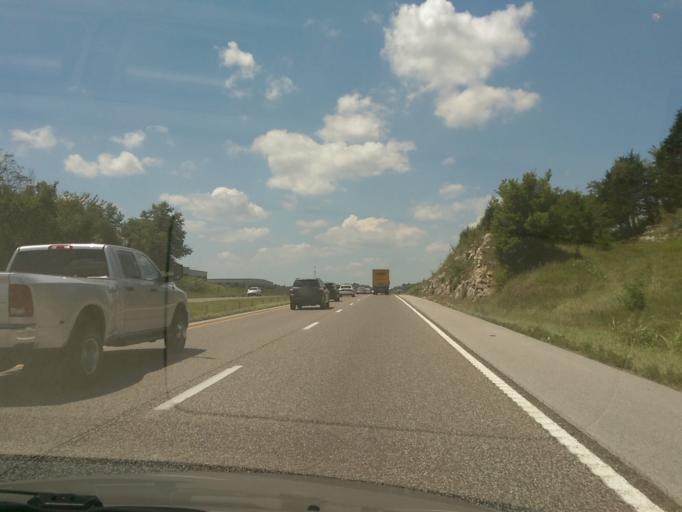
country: US
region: Missouri
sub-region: Boone County
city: Columbia
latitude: 38.9715
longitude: -92.4193
